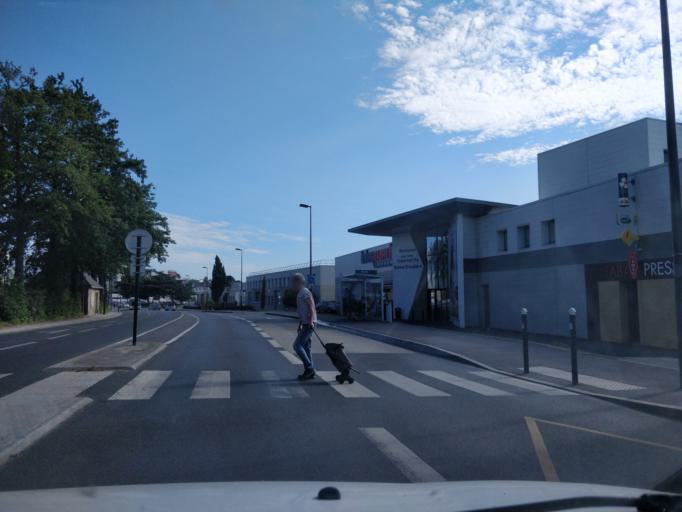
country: FR
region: Pays de la Loire
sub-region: Departement de la Loire-Atlantique
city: Nantes
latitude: 47.2447
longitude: -1.5335
